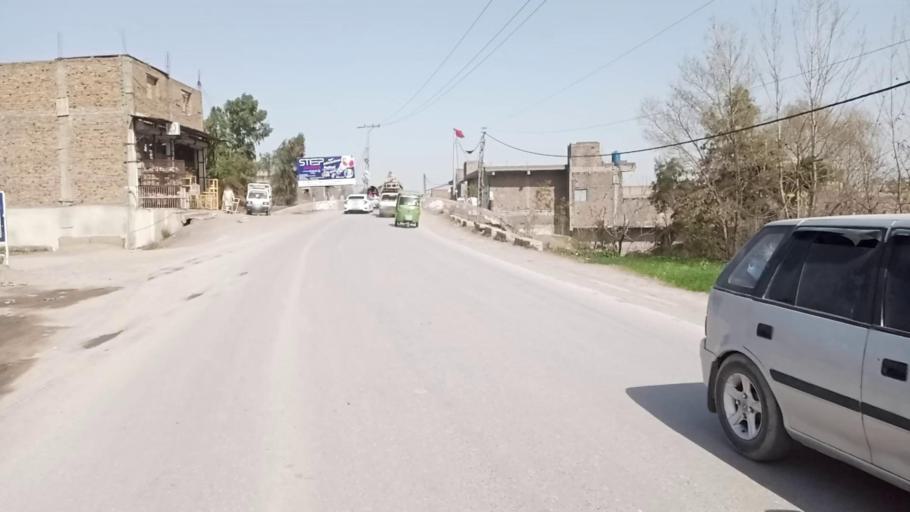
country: PK
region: Khyber Pakhtunkhwa
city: Peshawar
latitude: 34.0150
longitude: 71.6467
